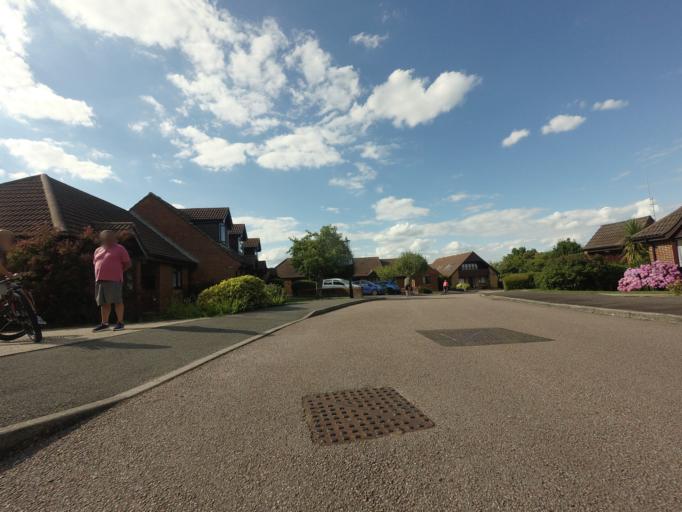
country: GB
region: England
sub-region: East Sussex
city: Hailsham
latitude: 50.8699
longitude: 0.2524
